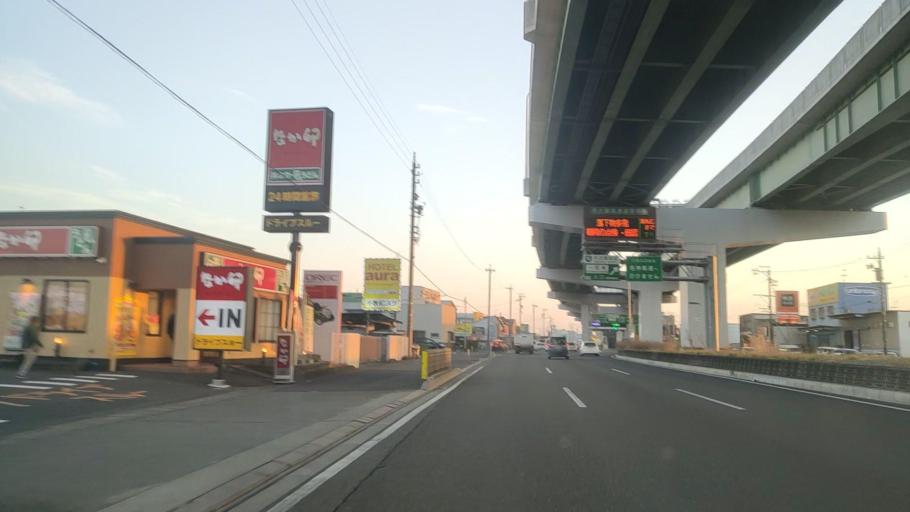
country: JP
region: Aichi
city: Ichinomiya
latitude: 35.2864
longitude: 136.8299
